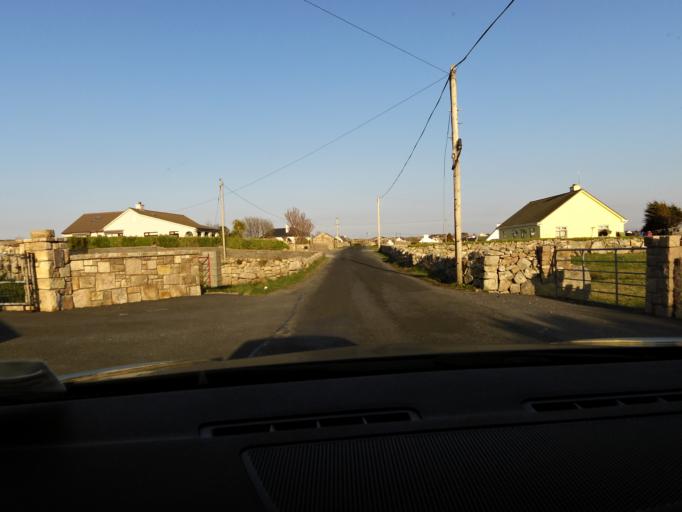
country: IE
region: Connaught
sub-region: County Galway
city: Oughterard
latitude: 53.2467
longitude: -9.5369
